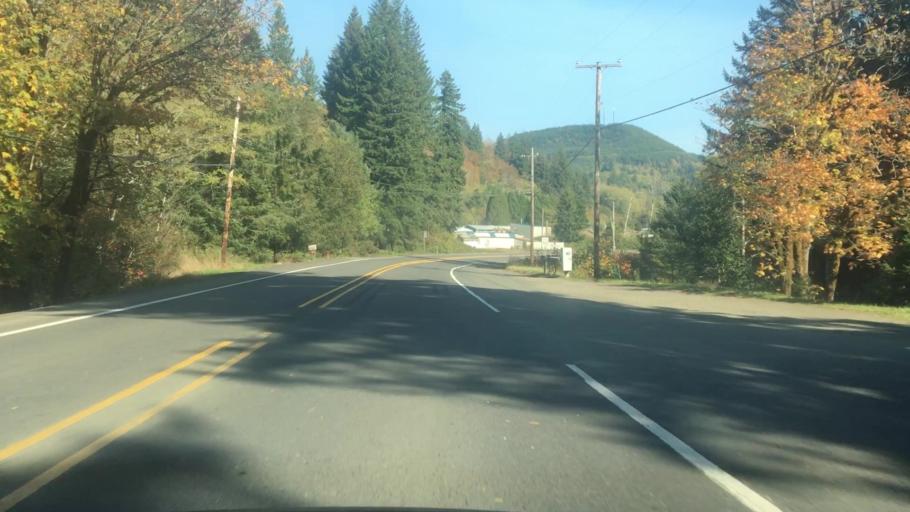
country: US
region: Oregon
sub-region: Lincoln County
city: Rose Lodge
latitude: 45.0206
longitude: -123.8631
